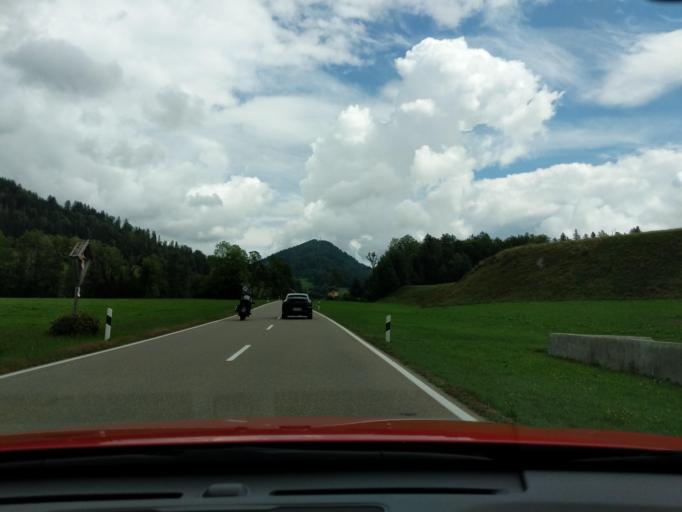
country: DE
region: Bavaria
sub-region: Swabia
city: Oberstaufen
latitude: 47.5376
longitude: 10.0032
